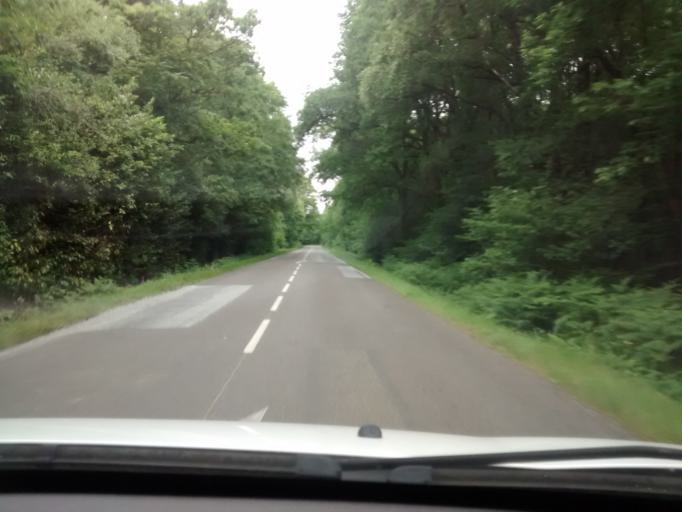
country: FR
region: Brittany
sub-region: Departement d'Ille-et-Vilaine
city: Servon-sur-Vilaine
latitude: 48.1421
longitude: -1.4494
